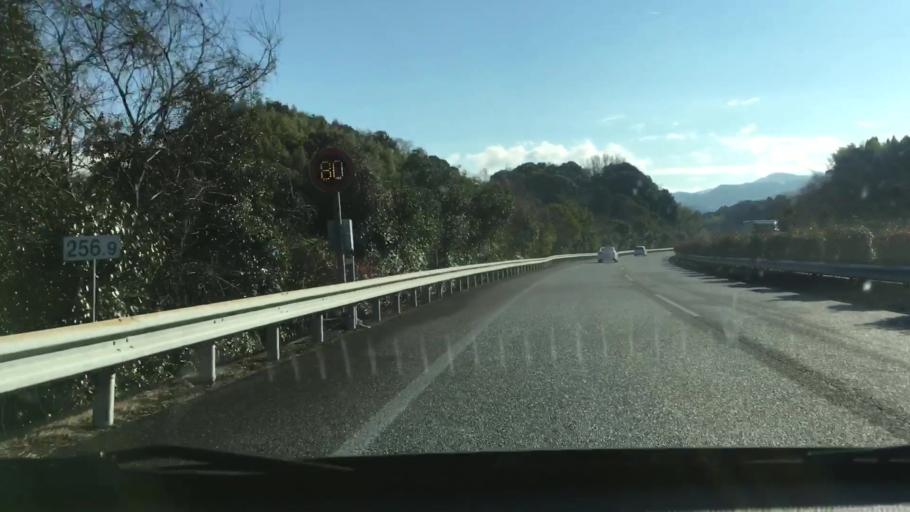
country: JP
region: Kumamoto
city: Hitoyoshi
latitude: 32.1946
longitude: 130.7779
